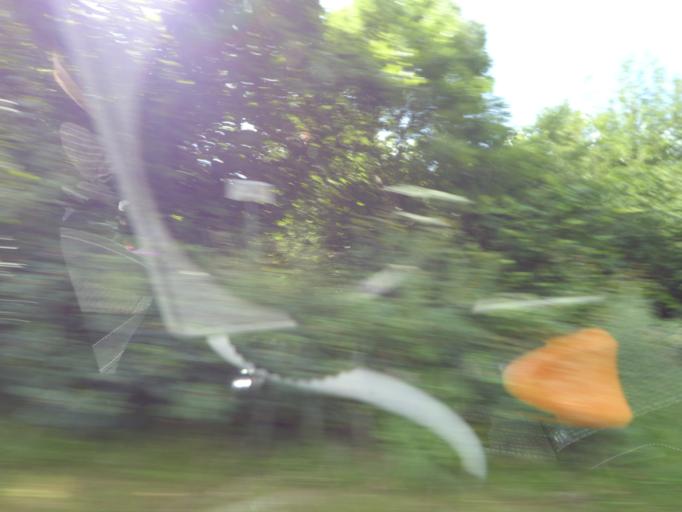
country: DK
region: South Denmark
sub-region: Assens Kommune
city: Arup
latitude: 55.3707
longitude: 10.0373
